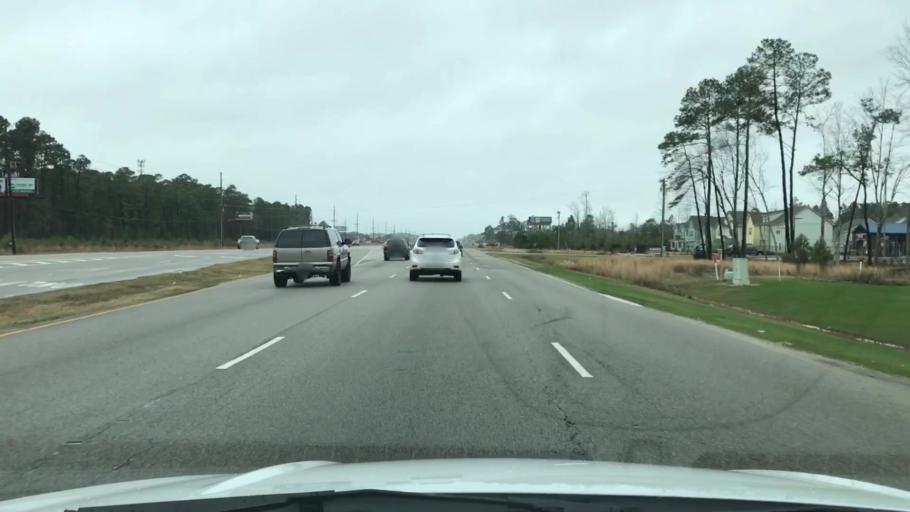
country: US
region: South Carolina
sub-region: Horry County
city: Red Hill
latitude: 33.7827
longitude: -78.9895
